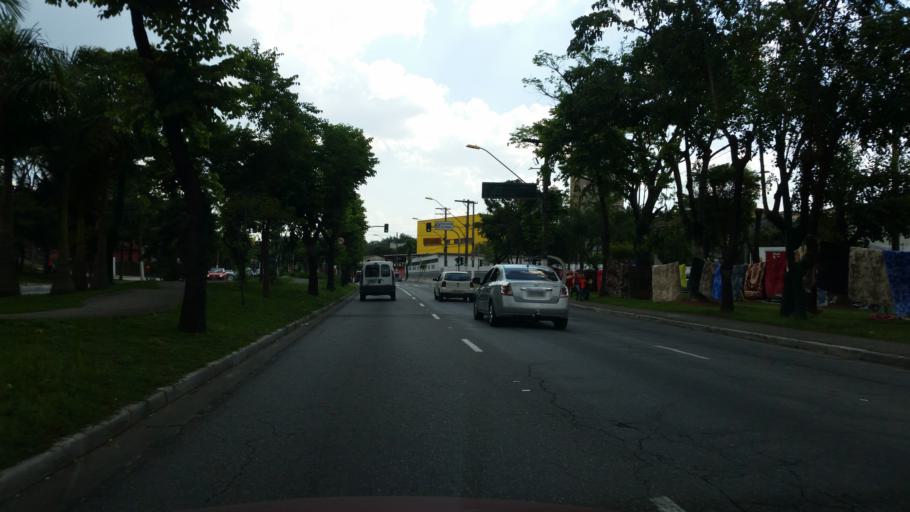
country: BR
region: Sao Paulo
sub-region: Santo Andre
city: Santo Andre
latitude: -23.6474
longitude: -46.5453
